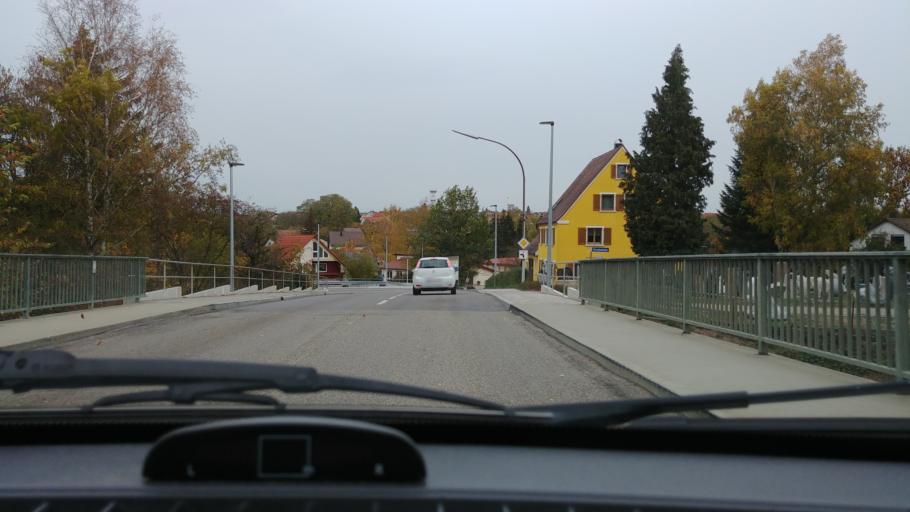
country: DE
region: Baden-Wuerttemberg
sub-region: Regierungsbezirk Stuttgart
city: Wallhausen
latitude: 49.2086
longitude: 10.0647
